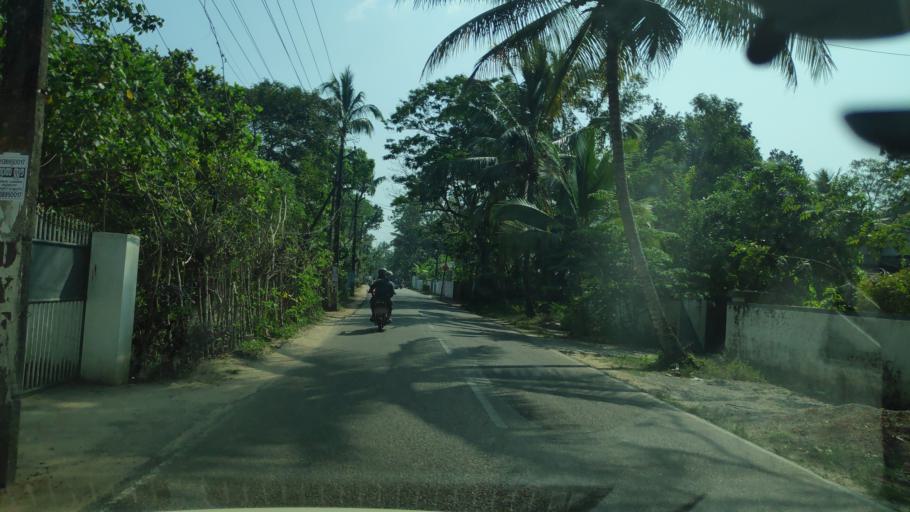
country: IN
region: Kerala
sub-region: Alappuzha
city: Vayalar
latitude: 9.6532
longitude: 76.2995
